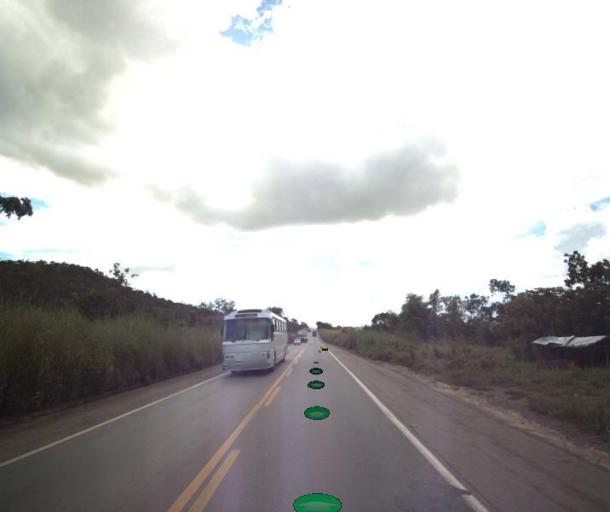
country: BR
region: Goias
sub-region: Jaragua
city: Jaragua
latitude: -15.8882
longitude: -49.2410
